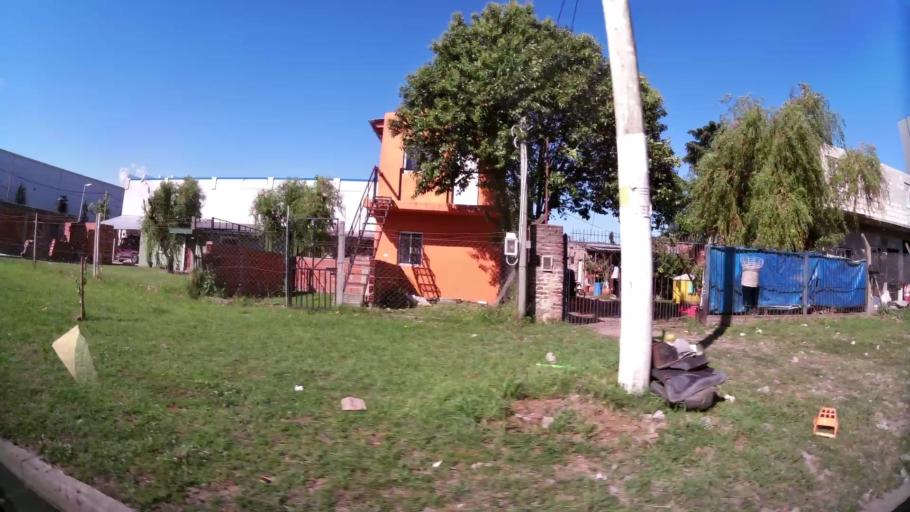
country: AR
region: Buenos Aires
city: Santa Catalina - Dique Lujan
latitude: -34.4670
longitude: -58.7116
